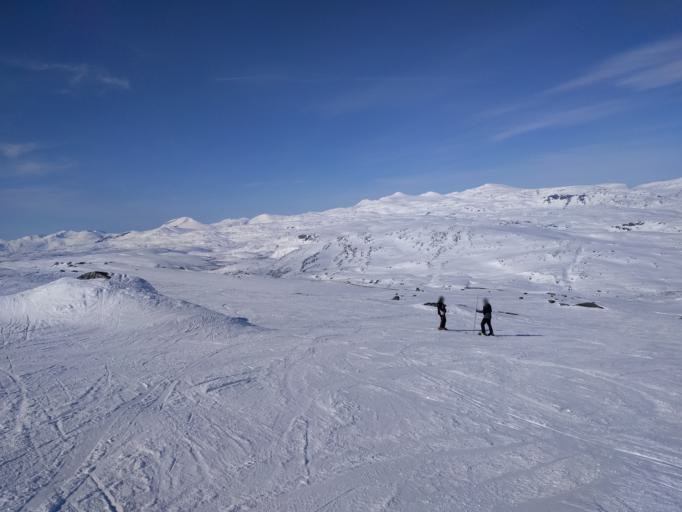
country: NO
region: Troms
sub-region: Lavangen
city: Tennevoll
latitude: 68.4194
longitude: 18.1019
